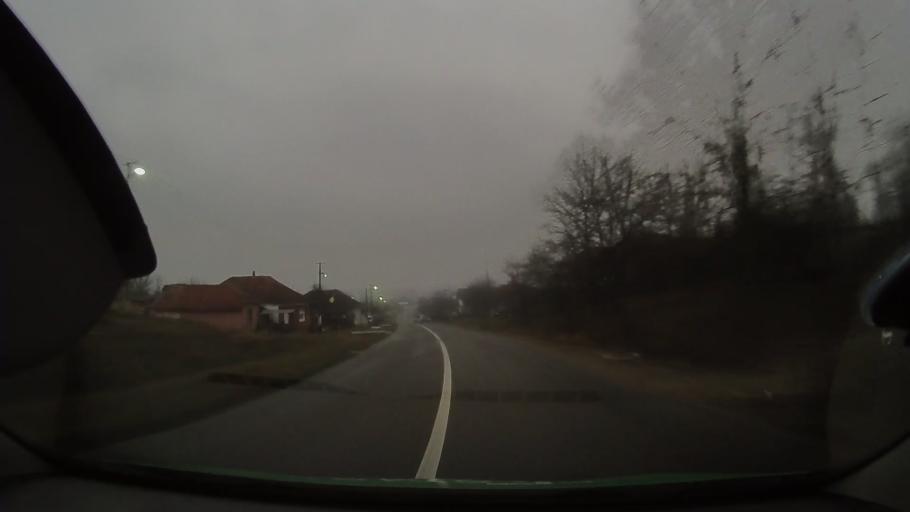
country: RO
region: Arad
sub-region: Comuna Beliu
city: Beliu
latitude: 46.4975
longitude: 21.9749
